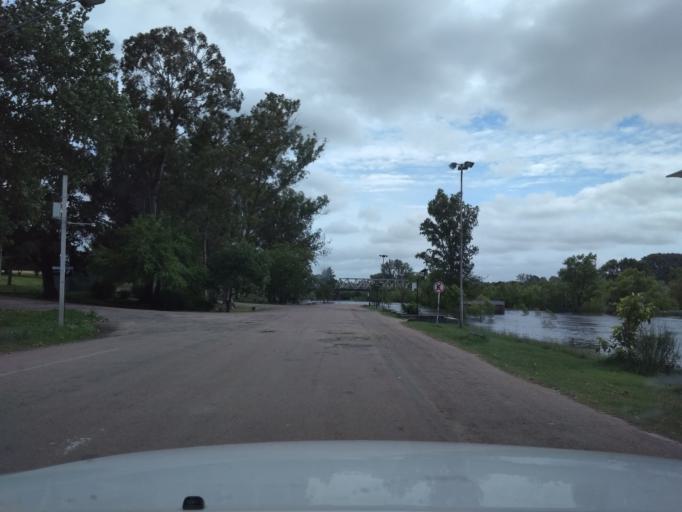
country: UY
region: Florida
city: Florida
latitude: -34.1021
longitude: -56.2035
